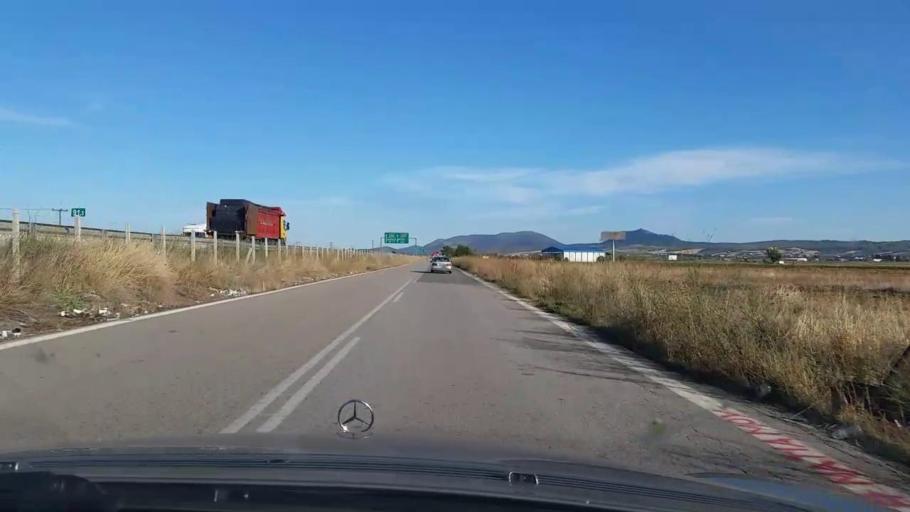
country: GR
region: Central Greece
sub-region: Nomos Voiotias
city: Thivai
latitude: 38.3666
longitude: 23.3042
